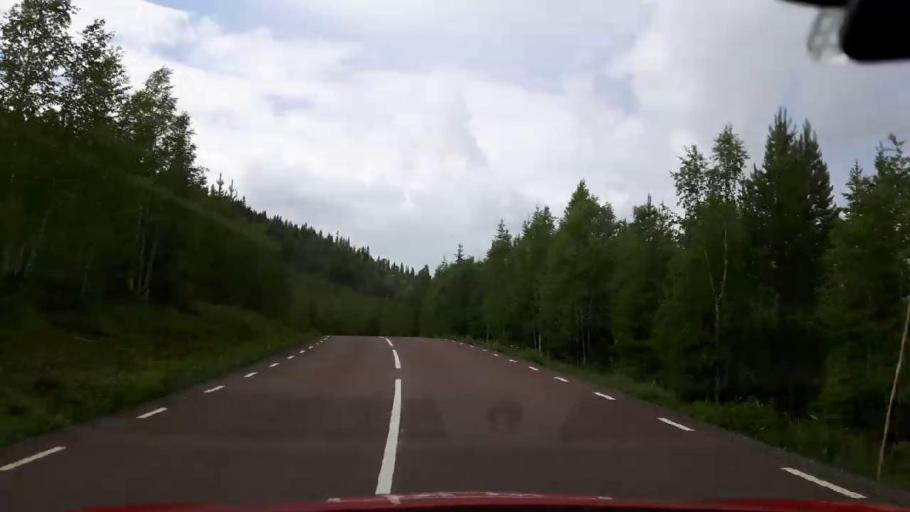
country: SE
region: Jaemtland
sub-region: Krokoms Kommun
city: Valla
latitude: 63.9478
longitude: 14.2232
